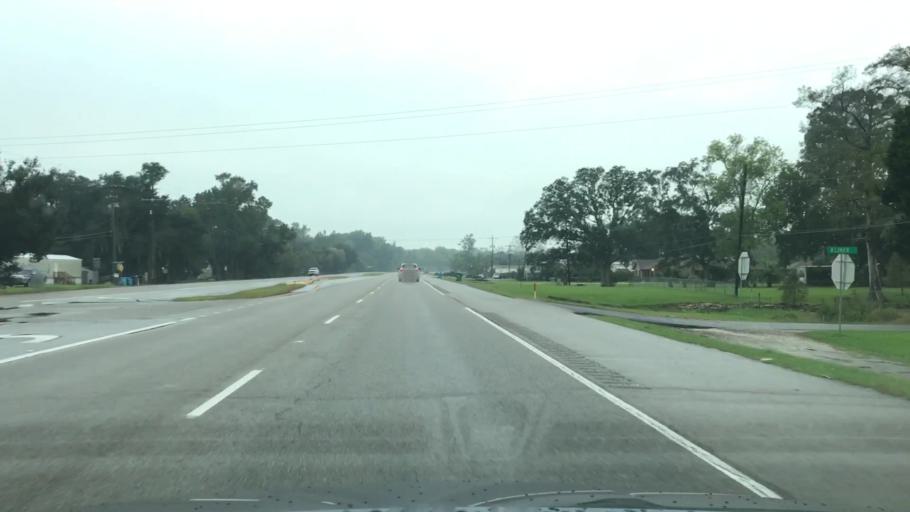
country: US
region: Louisiana
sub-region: Saint Charles Parish
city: Des Allemands
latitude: 29.8350
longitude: -90.4535
